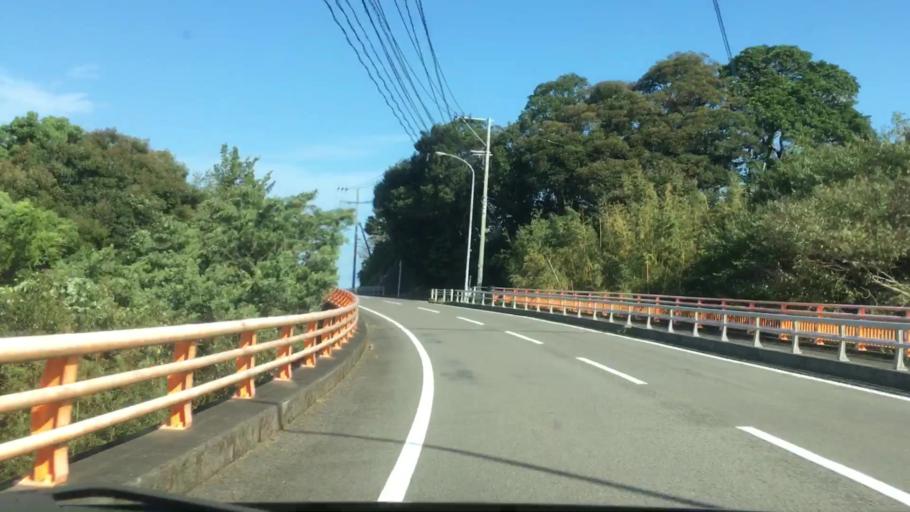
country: JP
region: Nagasaki
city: Sasebo
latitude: 33.0084
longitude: 129.6571
